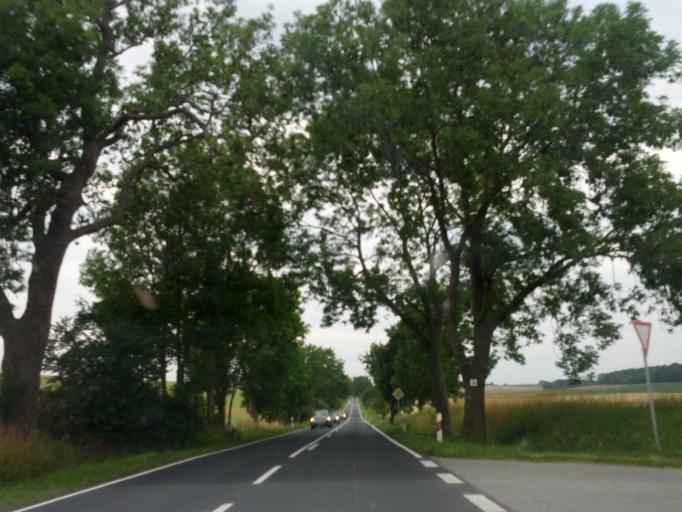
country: DE
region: Mecklenburg-Vorpommern
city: Satow-Oberhagen
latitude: 53.9808
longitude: 11.8610
